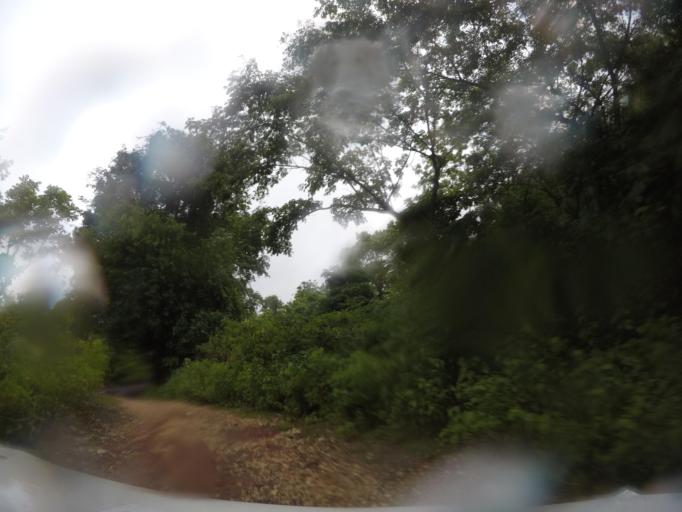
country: TL
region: Baucau
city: Venilale
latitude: -8.6282
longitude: 126.4322
